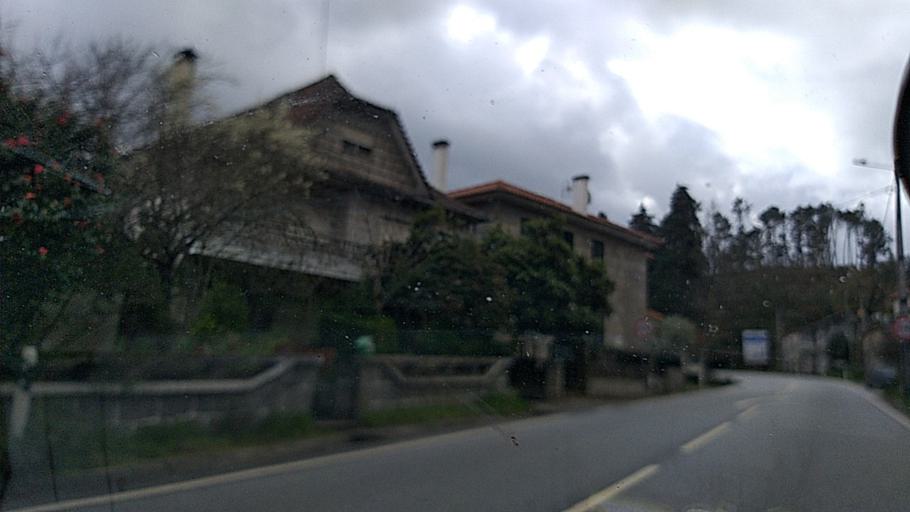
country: PT
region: Viseu
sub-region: Mangualde
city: Mangualde
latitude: 40.6370
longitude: -7.7402
